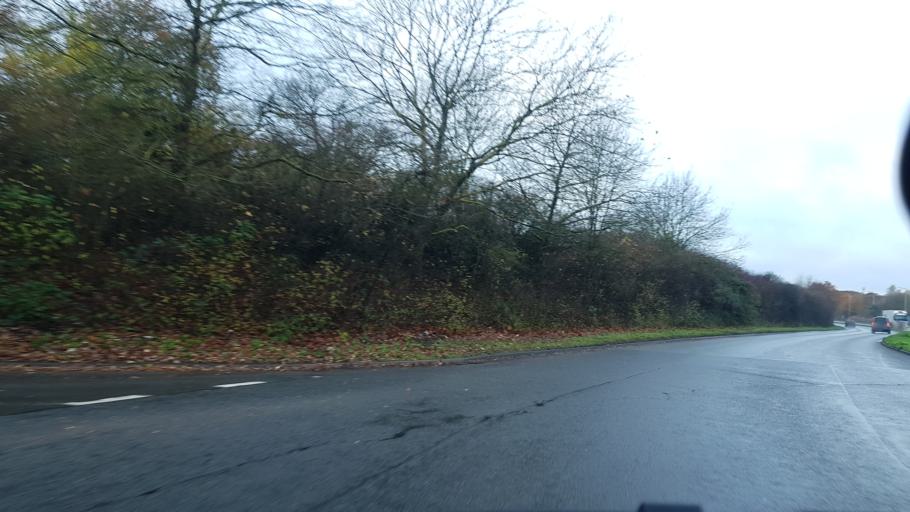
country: GB
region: England
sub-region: Bracknell Forest
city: Binfield
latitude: 51.4128
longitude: -0.7748
